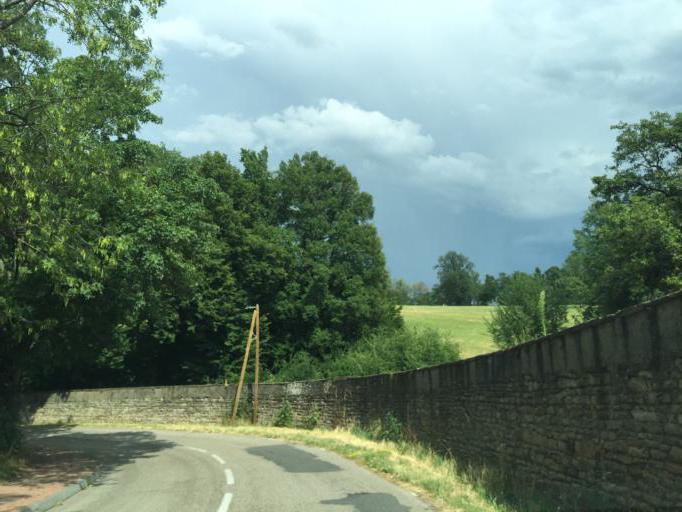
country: FR
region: Rhone-Alpes
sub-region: Departement de la Loire
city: Saint-Jean-Bonnefonds
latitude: 45.4439
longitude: 4.4495
